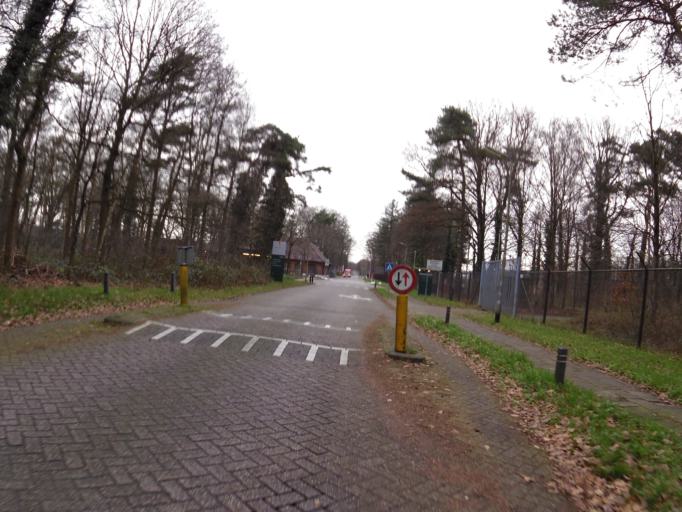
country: NL
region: North Brabant
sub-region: Gemeente Vught
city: Vught
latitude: 51.6584
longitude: 5.2597
